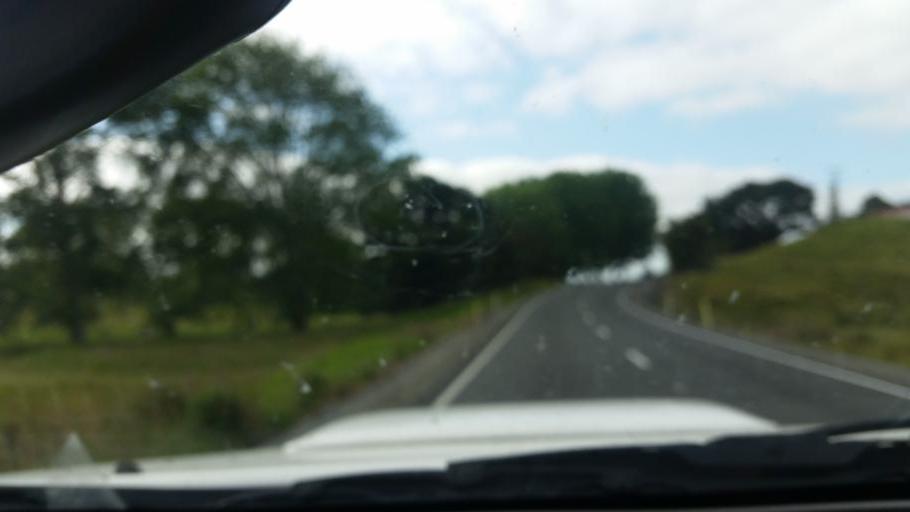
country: NZ
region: Northland
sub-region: Kaipara District
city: Dargaville
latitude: -35.8434
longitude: 173.8438
